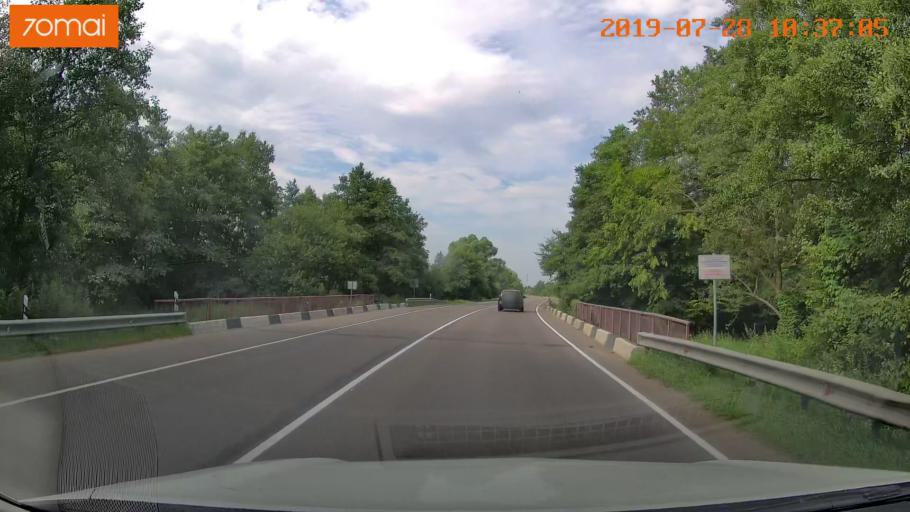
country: RU
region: Kaliningrad
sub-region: Gorod Kaliningrad
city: Kaliningrad
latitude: 54.7335
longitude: 20.4137
